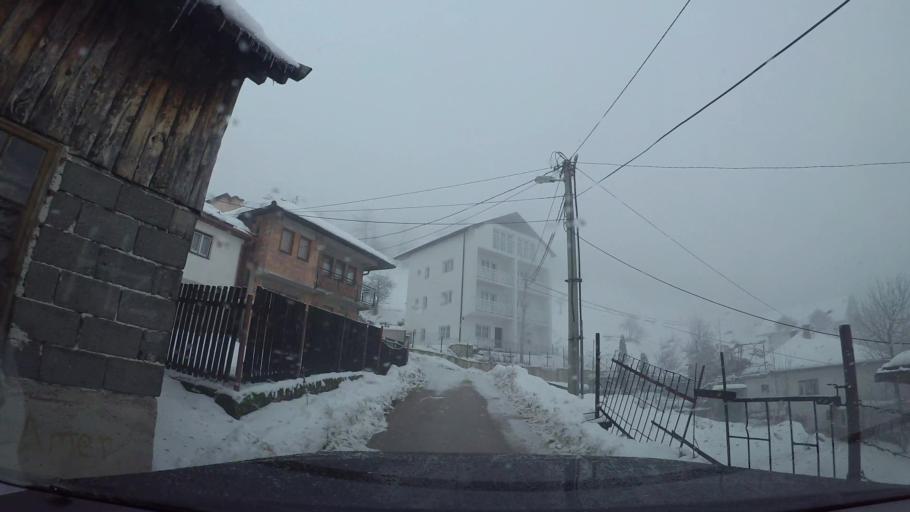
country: BA
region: Federation of Bosnia and Herzegovina
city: Kobilja Glava
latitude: 43.8501
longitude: 18.4441
